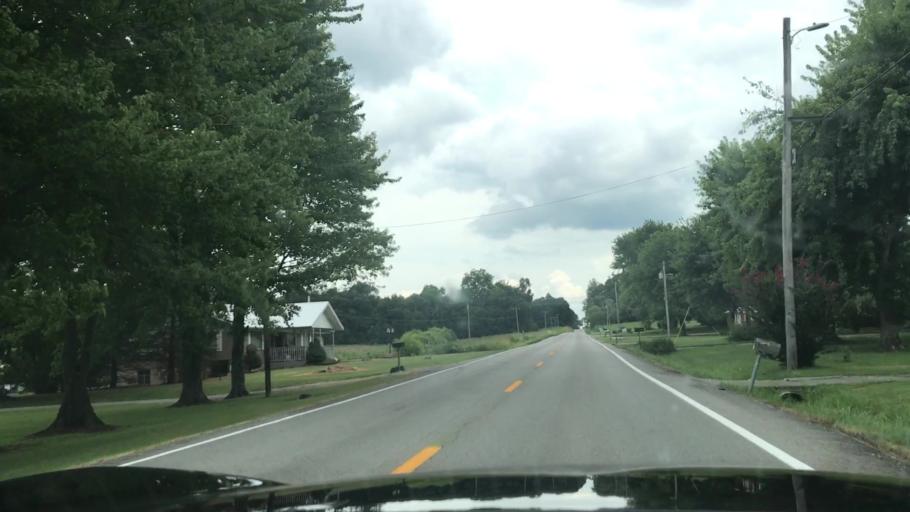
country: US
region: Kentucky
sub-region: Muhlenberg County
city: Central City
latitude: 37.2007
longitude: -87.0058
